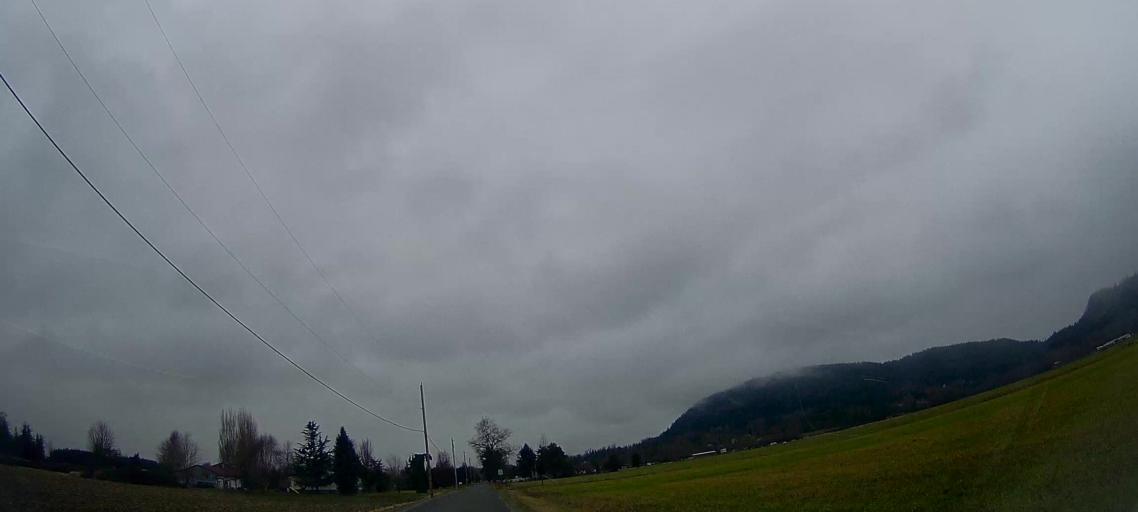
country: US
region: Washington
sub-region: Skagit County
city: Mount Vernon
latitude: 48.3724
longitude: -122.3240
